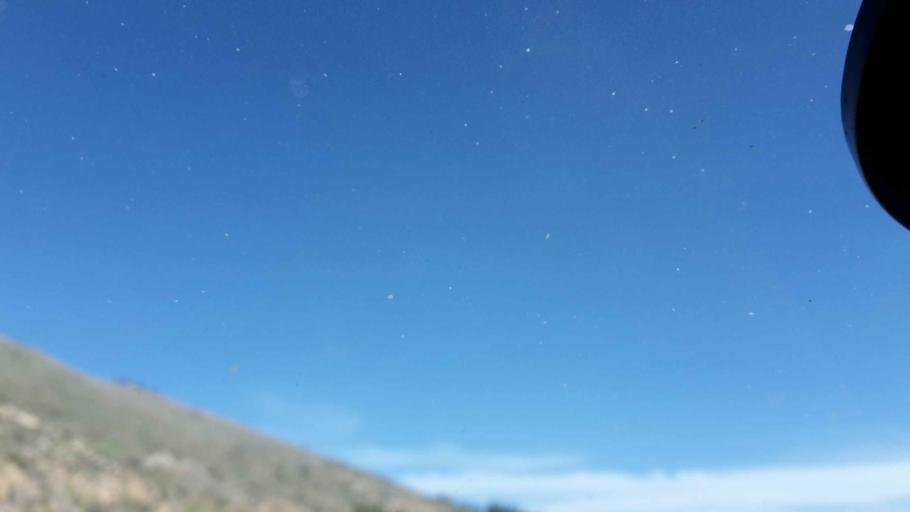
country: BO
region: Cochabamba
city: Arani
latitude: -17.6853
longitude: -65.7226
